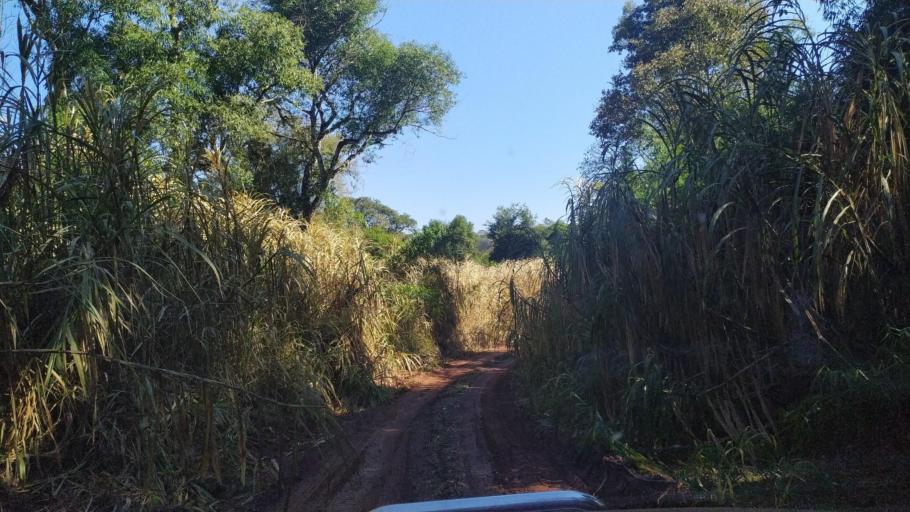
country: AR
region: Misiones
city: El Alcazar
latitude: -26.7545
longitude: -54.5989
